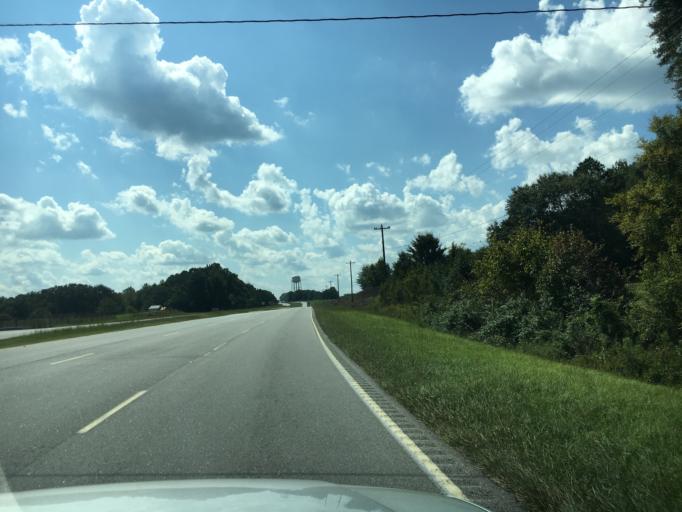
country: US
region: South Carolina
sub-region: Spartanburg County
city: Woodruff
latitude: 34.8085
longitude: -82.0058
